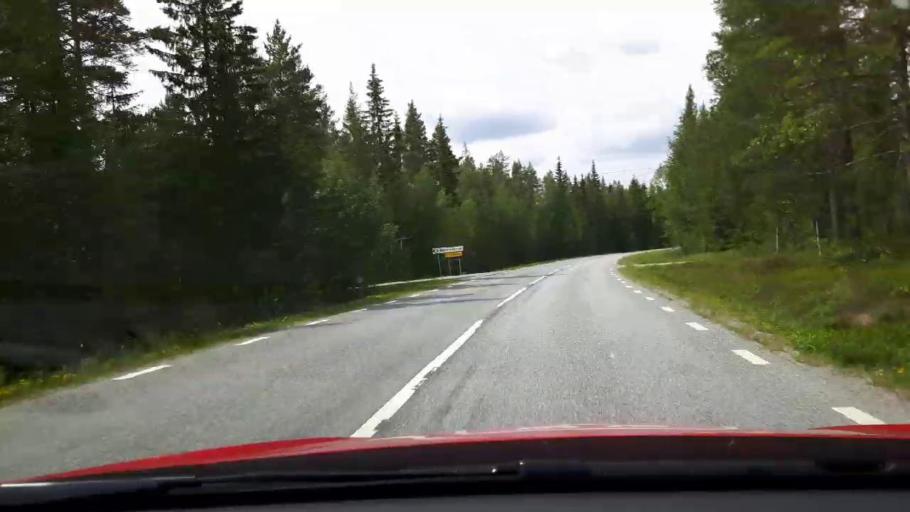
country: SE
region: Jaemtland
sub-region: Harjedalens Kommun
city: Sveg
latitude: 62.1474
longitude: 13.9122
